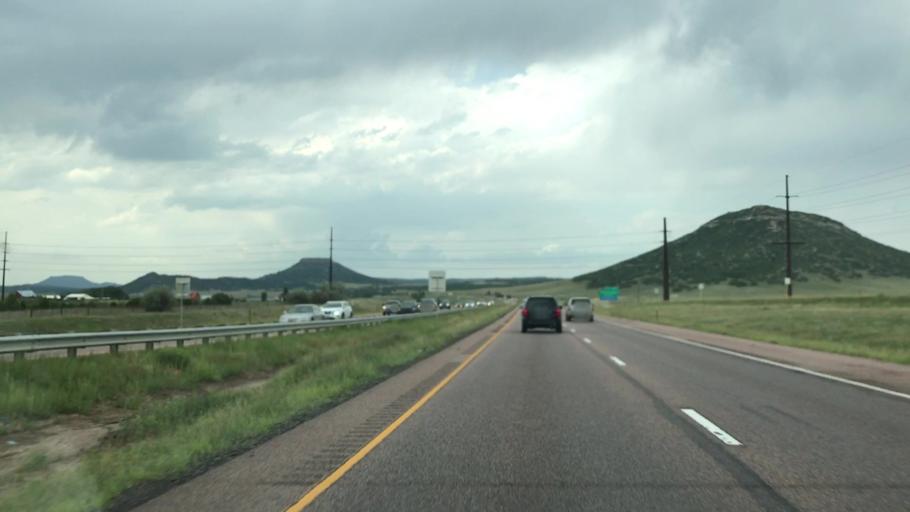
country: US
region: Colorado
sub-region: El Paso County
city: Woodmoor
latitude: 39.1781
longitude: -104.8501
